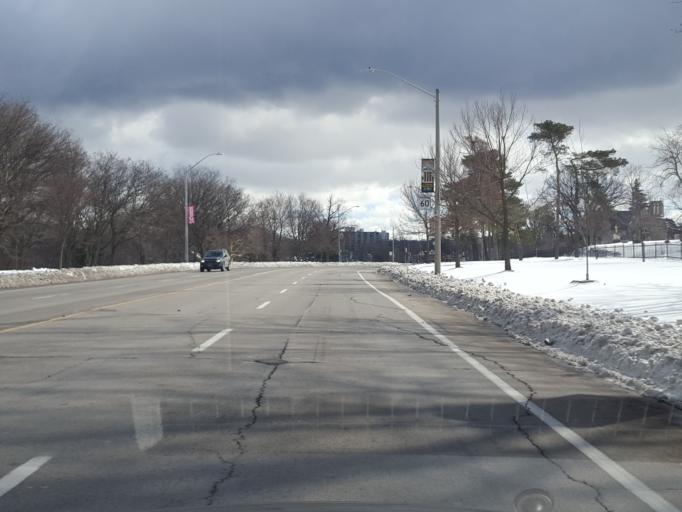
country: CA
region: Ontario
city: Hamilton
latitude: 43.2729
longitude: -79.8873
